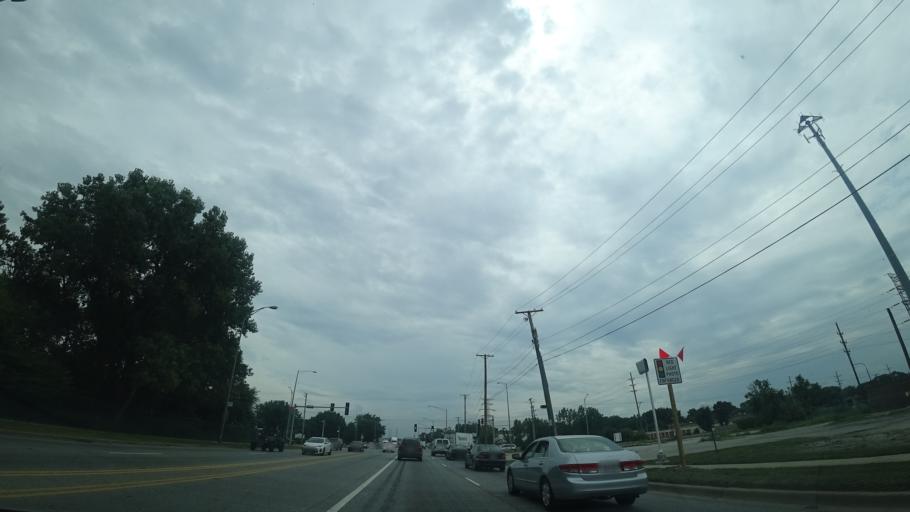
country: US
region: Illinois
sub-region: Cook County
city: Alsip
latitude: 41.6844
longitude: -87.7395
